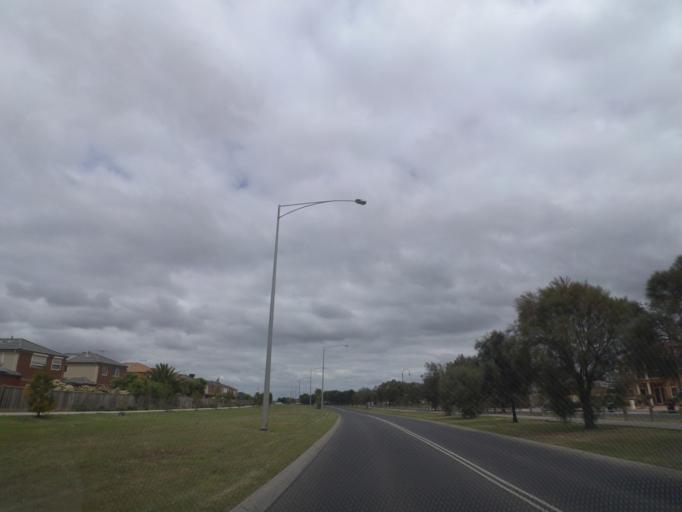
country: AU
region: Victoria
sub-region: Melton
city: Burnside Heights
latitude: -37.7203
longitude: 144.7512
